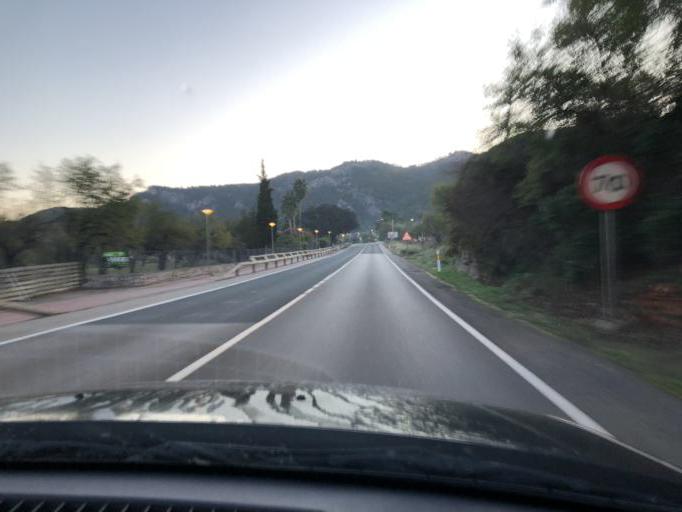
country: ES
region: Balearic Islands
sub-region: Illes Balears
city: Andratx
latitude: 39.5659
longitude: 2.4136
